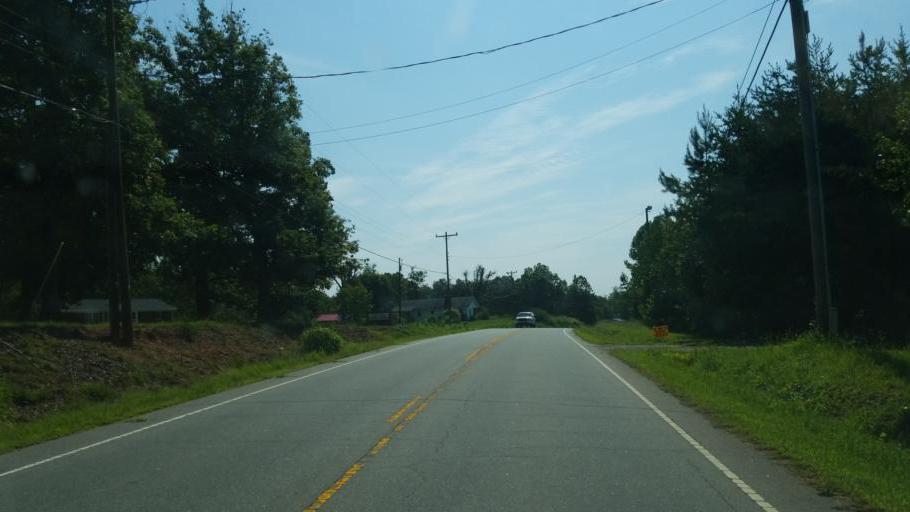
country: US
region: North Carolina
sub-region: Burke County
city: Glen Alpine
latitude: 35.8018
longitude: -81.7766
